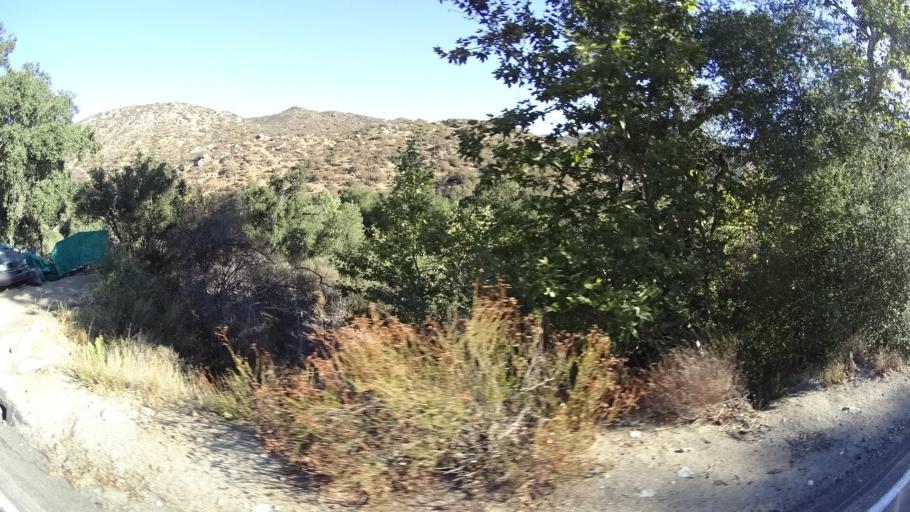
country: MX
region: Baja California
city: Tecate
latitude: 32.5934
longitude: -116.6660
